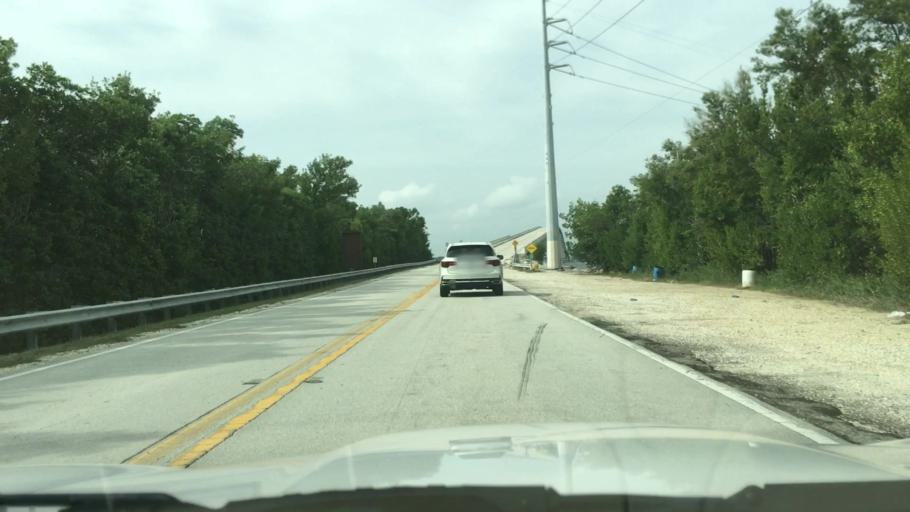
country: US
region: Florida
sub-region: Monroe County
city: North Key Largo
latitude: 25.2853
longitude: -80.3633
